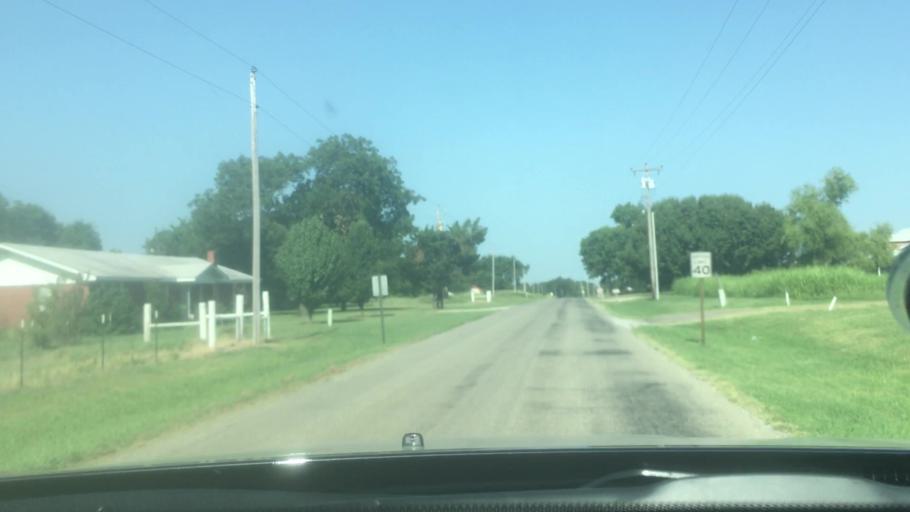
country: US
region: Oklahoma
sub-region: Bryan County
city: Calera
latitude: 33.9397
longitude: -96.4397
